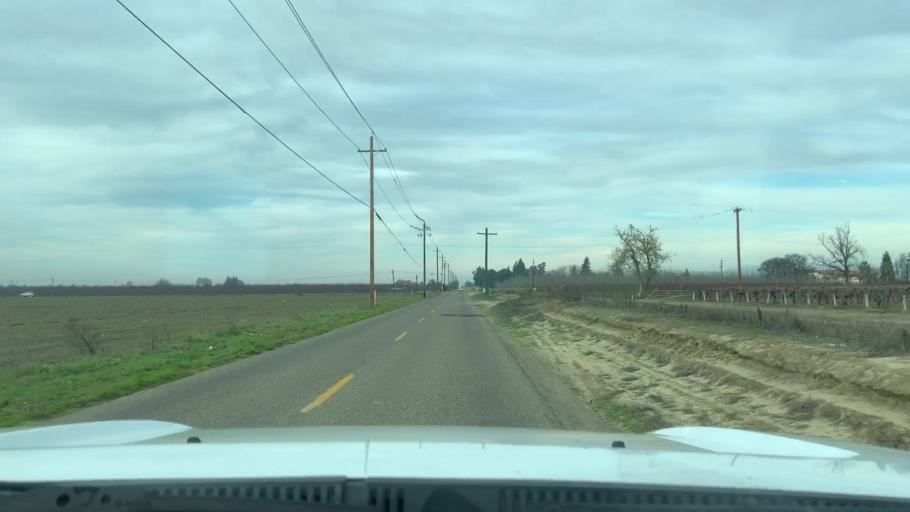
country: US
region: California
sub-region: Fresno County
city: Selma
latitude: 36.5736
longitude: -119.5750
